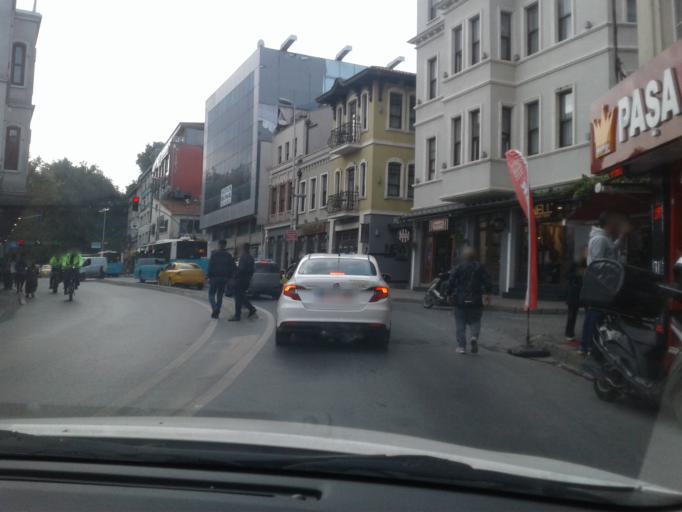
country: TR
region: Istanbul
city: UEskuedar
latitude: 41.0485
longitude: 29.0254
